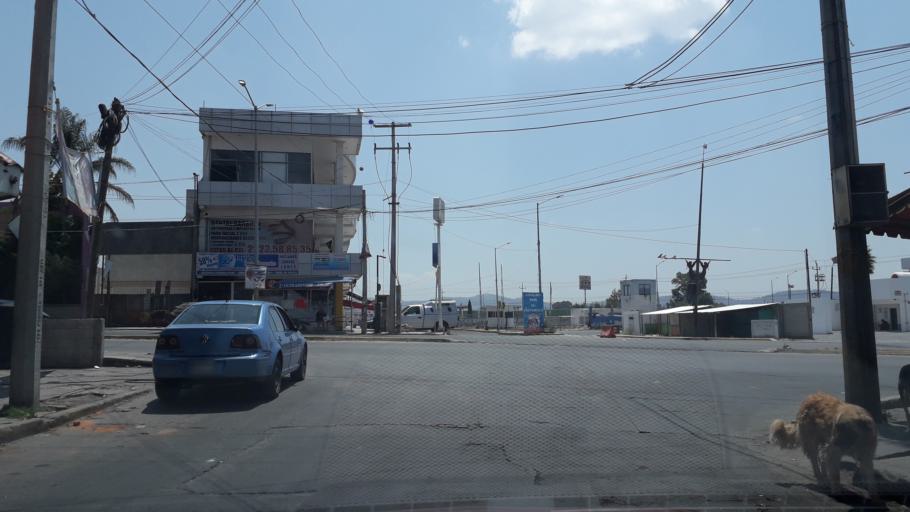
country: MX
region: Puebla
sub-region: Puebla
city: Primero de Mayo
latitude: 19.0687
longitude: -98.1177
